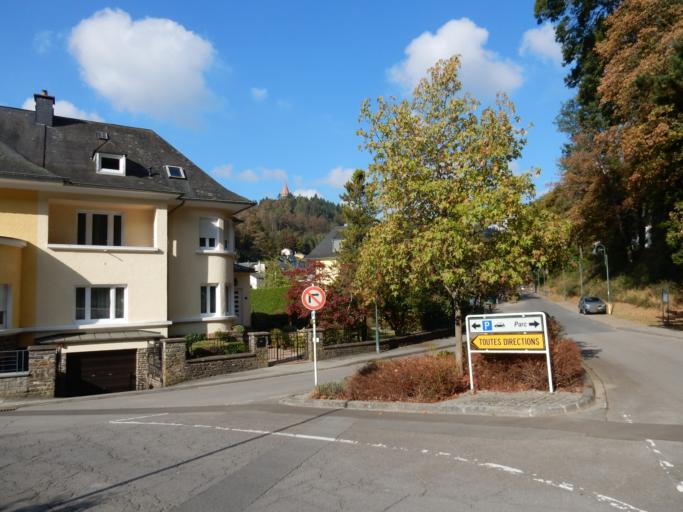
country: LU
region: Diekirch
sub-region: Canton de Clervaux
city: Clervaux
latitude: 50.0555
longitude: 6.0314
